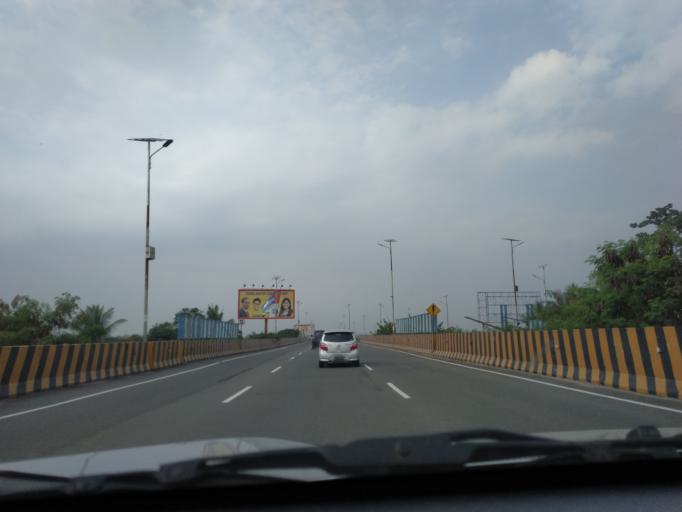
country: ID
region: North Sumatra
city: Percut
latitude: 3.6083
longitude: 98.8523
